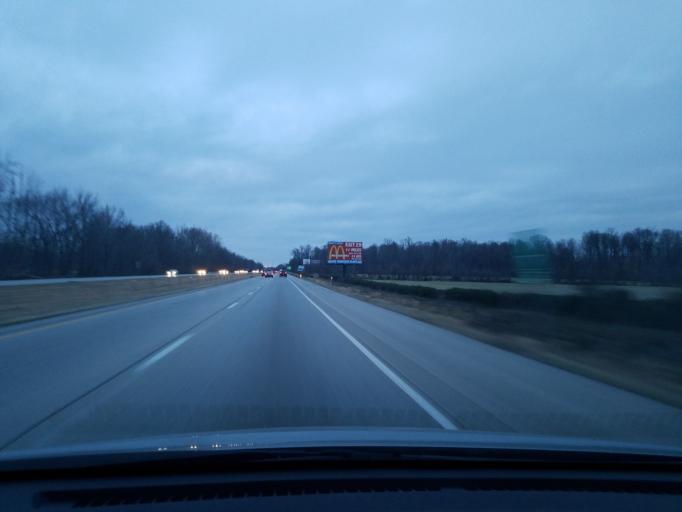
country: US
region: Indiana
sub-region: Clark County
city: Henryville
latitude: 38.5164
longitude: -85.7724
